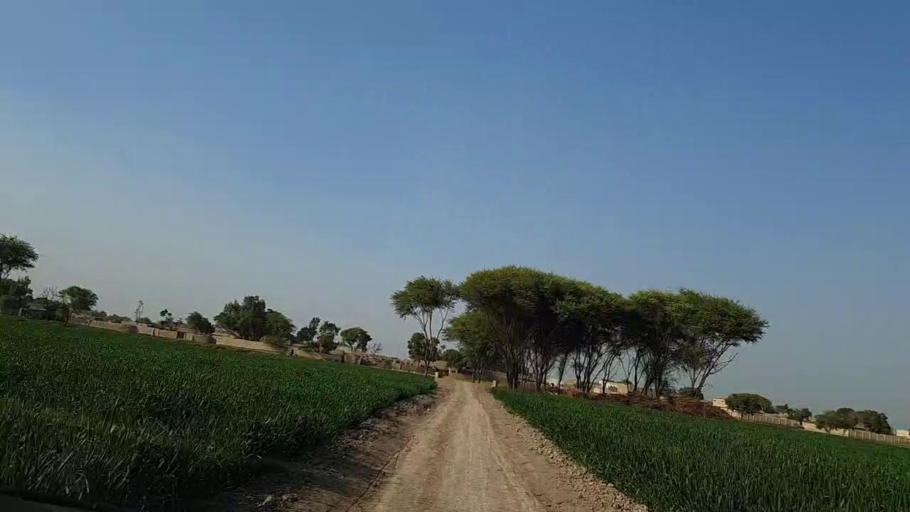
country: PK
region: Sindh
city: Sakrand
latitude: 26.1238
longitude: 68.2391
